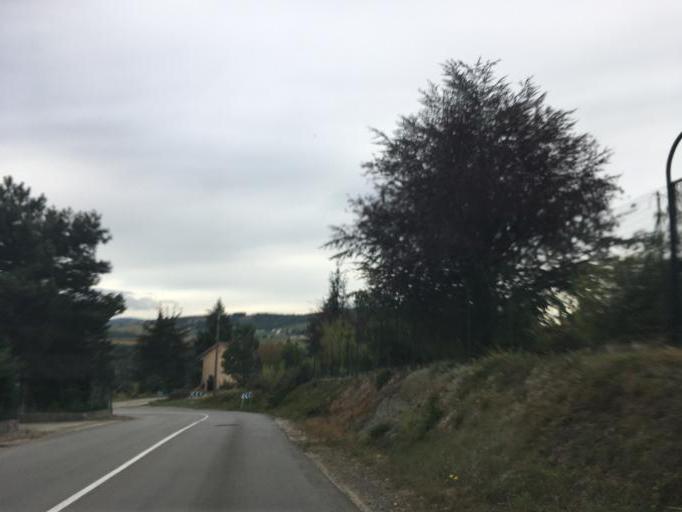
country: FR
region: Rhone-Alpes
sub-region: Departement de la Loire
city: Chateauneuf
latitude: 45.5423
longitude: 4.6349
